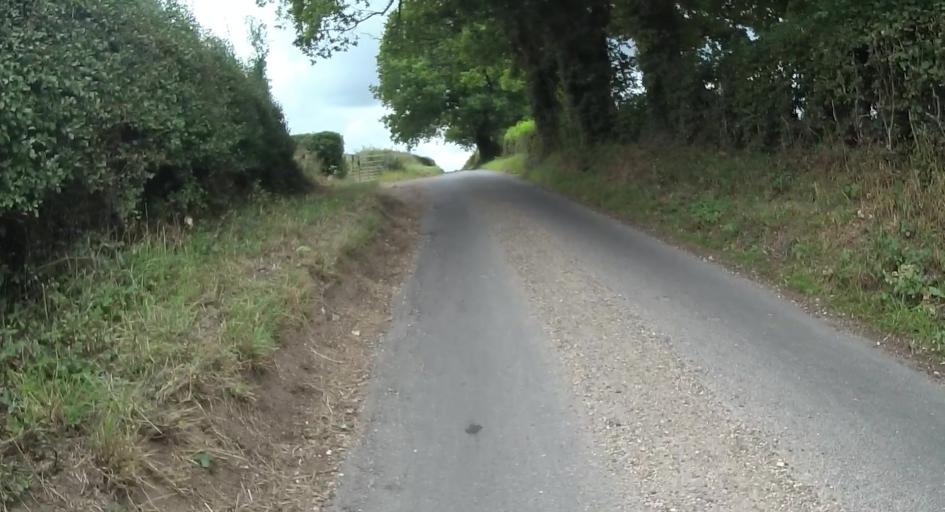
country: GB
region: England
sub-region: Hampshire
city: Four Marks
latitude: 51.1025
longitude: -1.1236
